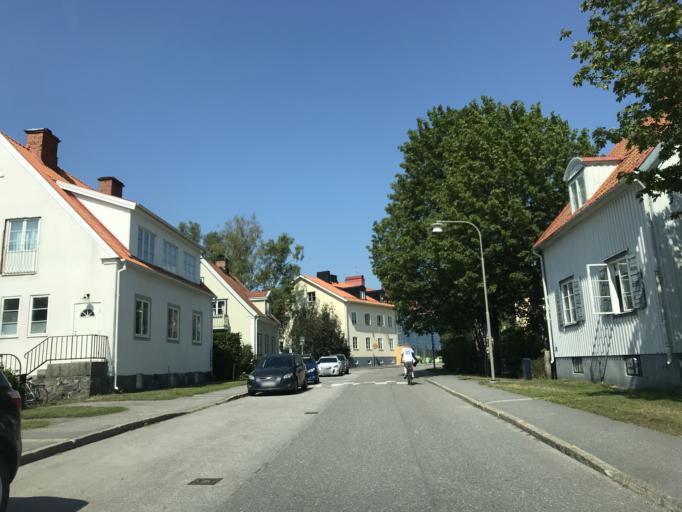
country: SE
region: Stockholm
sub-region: Stockholms Kommun
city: Bromma
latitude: 59.3277
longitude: 17.9702
